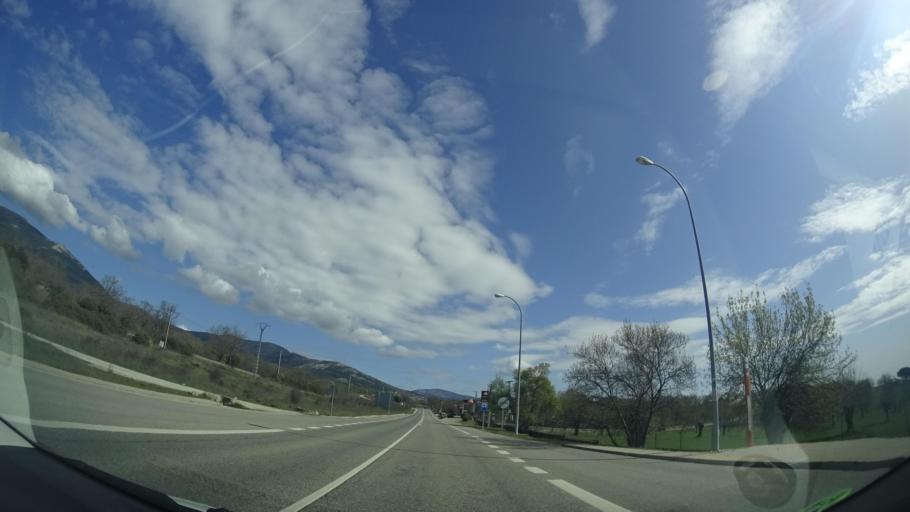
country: ES
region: Madrid
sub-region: Provincia de Madrid
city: Miraflores de la Sierra
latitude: 40.7793
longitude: -3.7750
